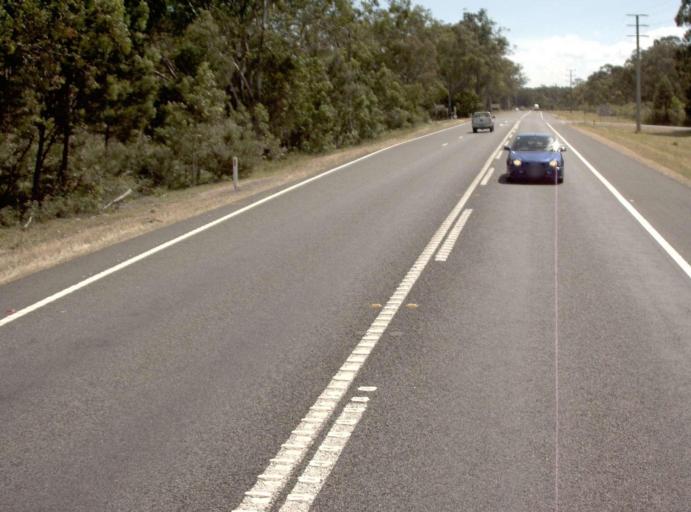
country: AU
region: Victoria
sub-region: East Gippsland
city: Bairnsdale
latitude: -37.9080
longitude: 147.3229
